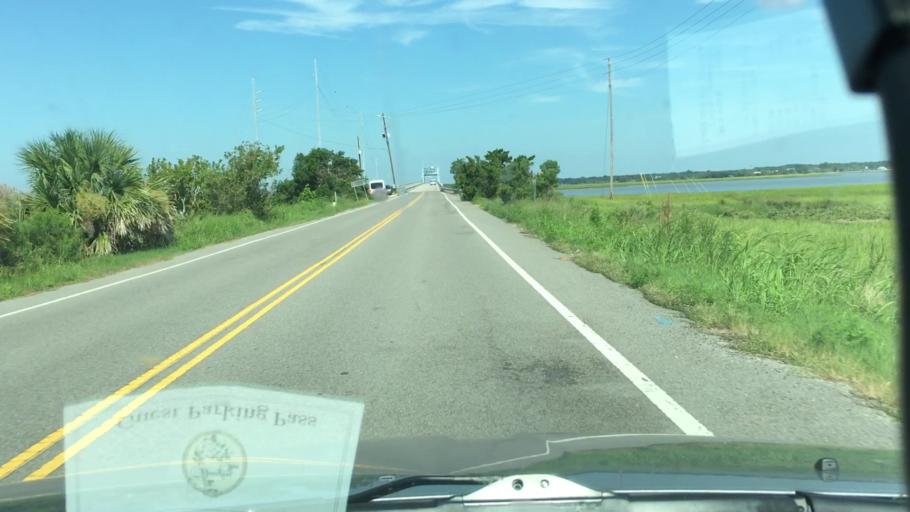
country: US
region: South Carolina
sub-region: Beaufort County
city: Beaufort
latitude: 32.4027
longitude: -80.4484
